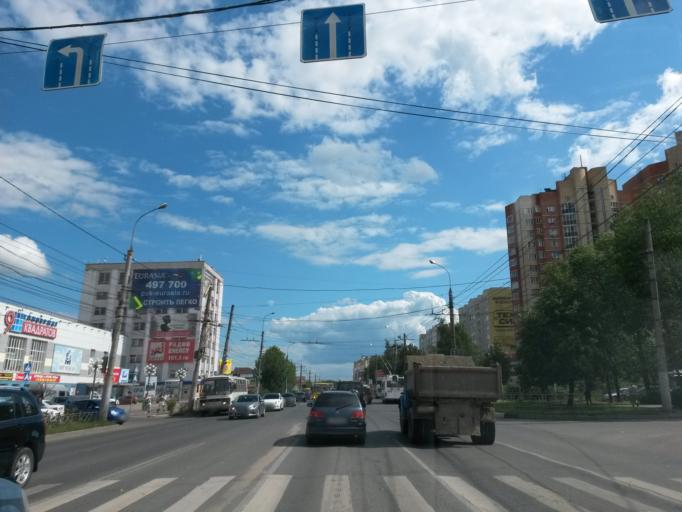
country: RU
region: Ivanovo
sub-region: Gorod Ivanovo
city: Ivanovo
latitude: 56.9659
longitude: 41.0212
